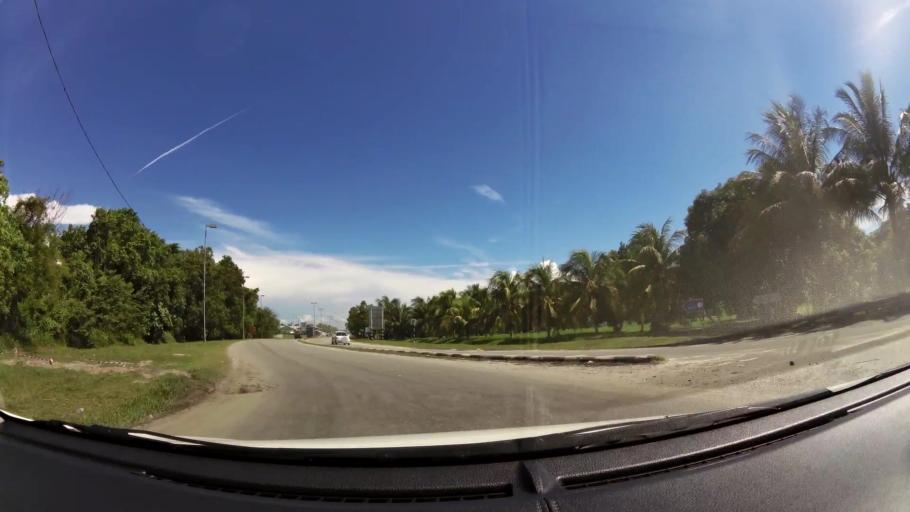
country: BN
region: Brunei and Muara
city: Bandar Seri Begawan
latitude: 5.0229
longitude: 115.0629
